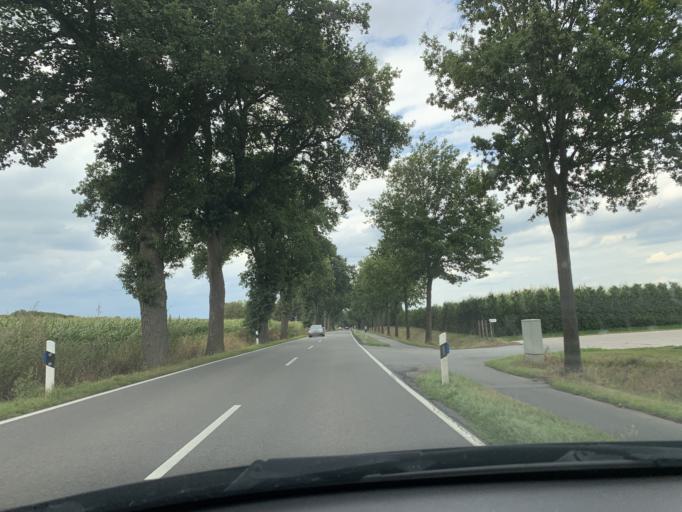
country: DE
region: Lower Saxony
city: Westerstede
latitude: 53.2307
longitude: 7.9026
